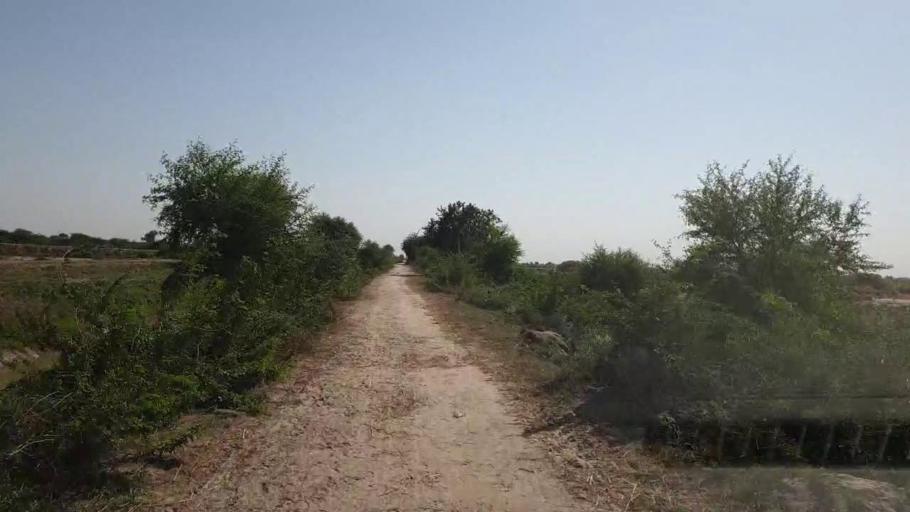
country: PK
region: Sindh
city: Kadhan
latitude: 24.6175
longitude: 68.9970
